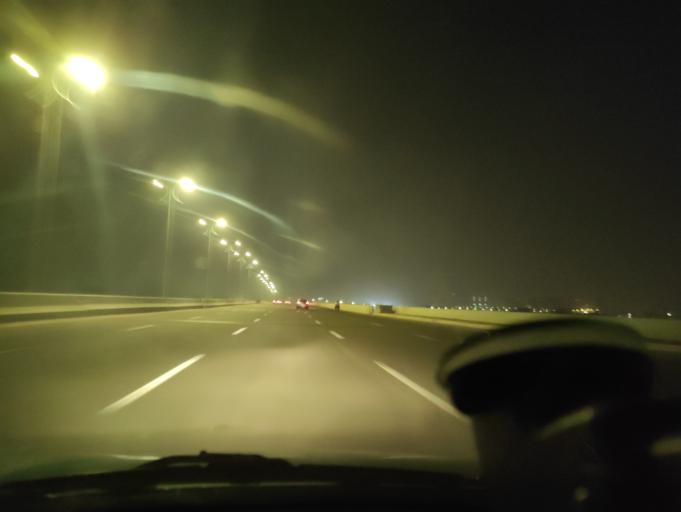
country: EG
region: Muhafazat al Qahirah
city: Cairo
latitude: 30.1116
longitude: 31.2158
